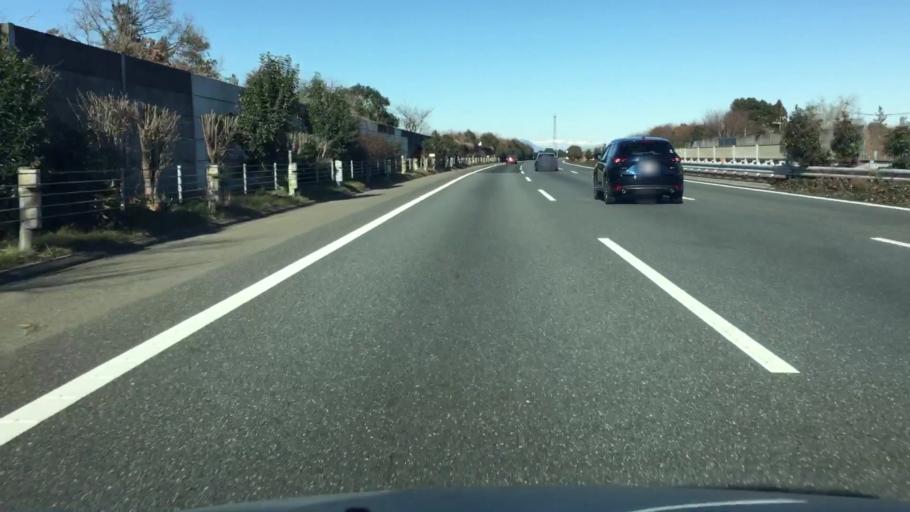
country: JP
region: Saitama
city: Yorii
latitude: 36.1377
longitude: 139.2278
